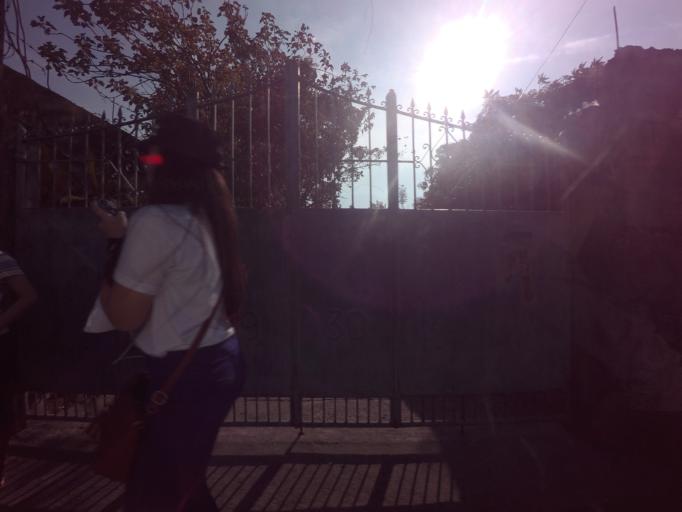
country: PH
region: Calabarzon
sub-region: Province of Rizal
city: Taguig
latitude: 14.4971
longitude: 121.0520
